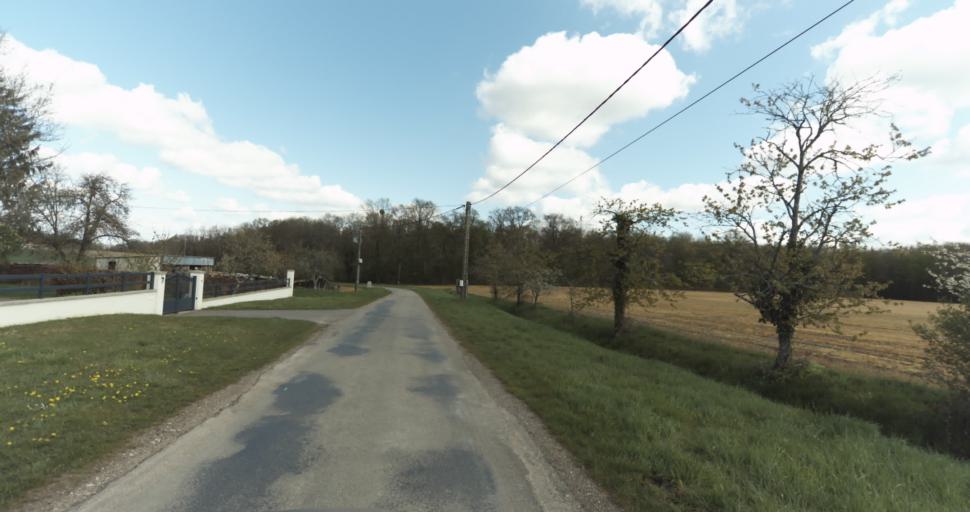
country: FR
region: Bourgogne
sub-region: Departement de la Cote-d'Or
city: Auxonne
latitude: 47.2104
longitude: 5.4323
